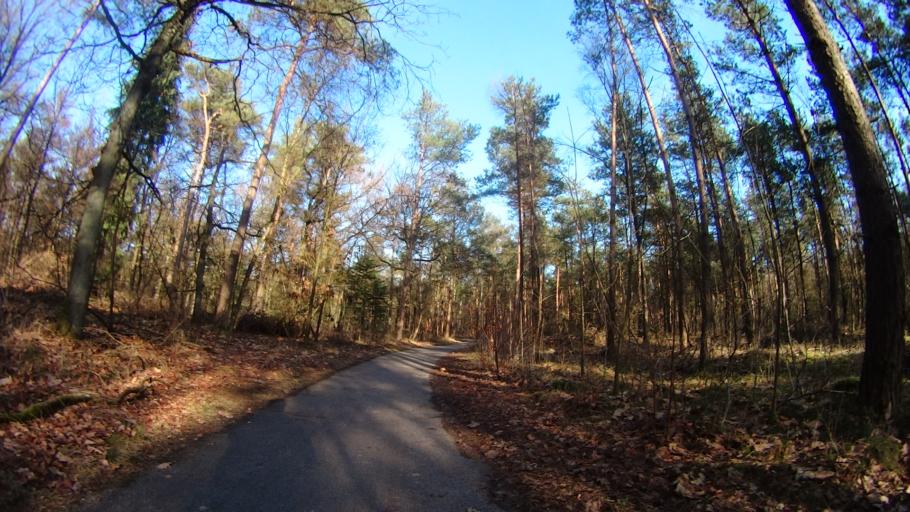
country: NL
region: Drenthe
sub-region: Gemeente Emmen
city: Emmen
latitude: 52.7761
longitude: 6.8597
